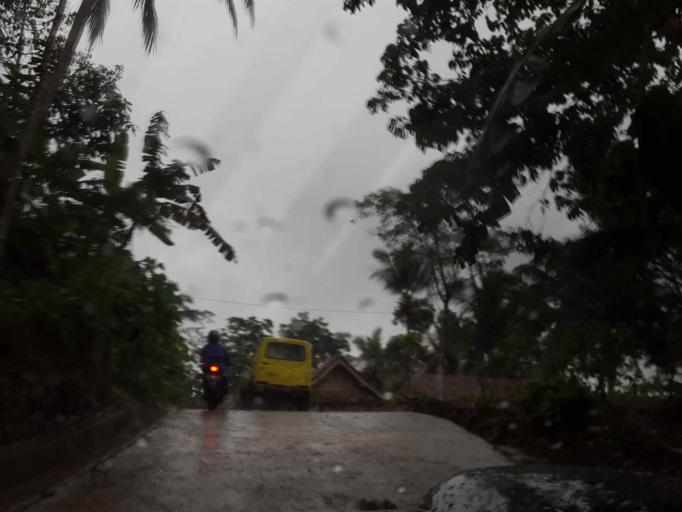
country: ID
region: Central Java
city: Kutoarjo
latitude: -7.5695
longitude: 109.7417
